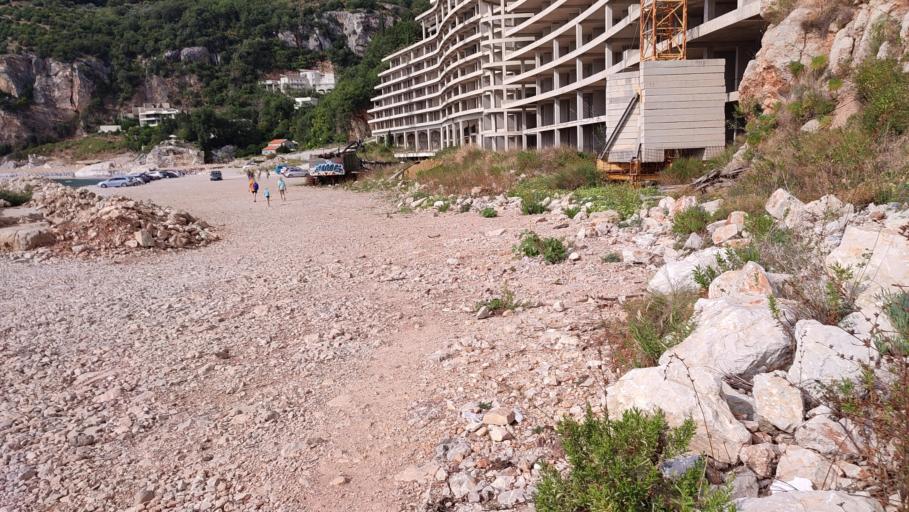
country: ME
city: Petrovac na Moru
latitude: 42.2095
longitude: 18.9262
